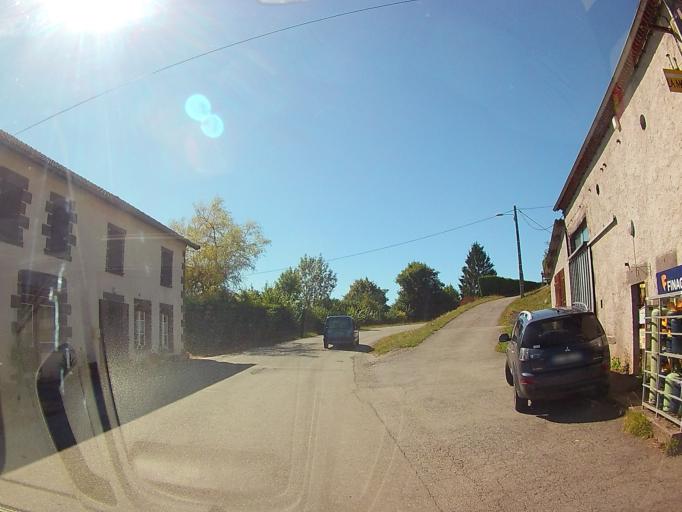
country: FR
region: Auvergne
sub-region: Departement du Puy-de-Dome
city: Manzat
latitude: 45.9141
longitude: 2.9393
